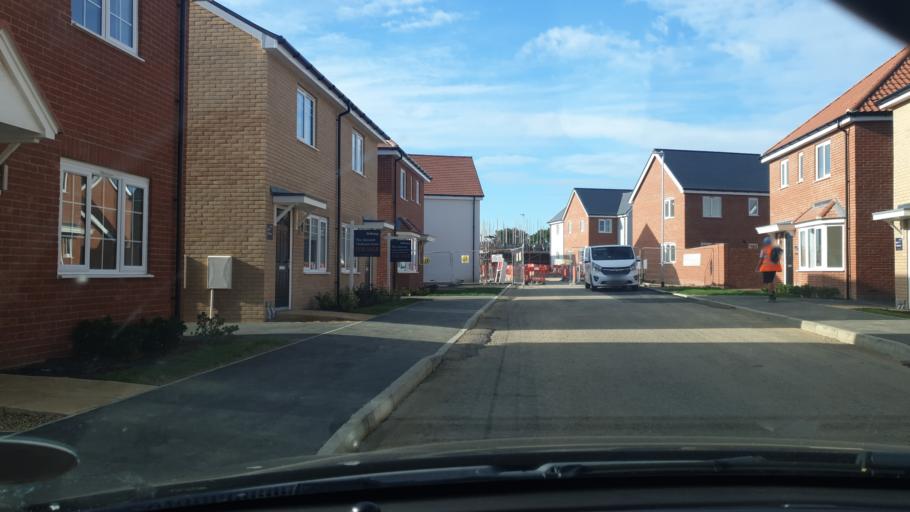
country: GB
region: England
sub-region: Essex
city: Little Clacton
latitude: 51.8591
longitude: 1.1728
